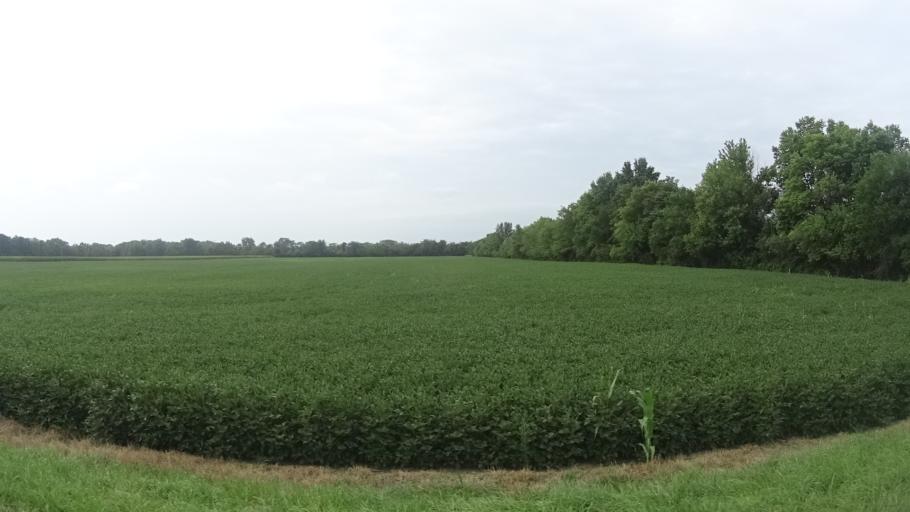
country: US
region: Indiana
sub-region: Madison County
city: Edgewood
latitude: 40.1020
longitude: -85.7839
